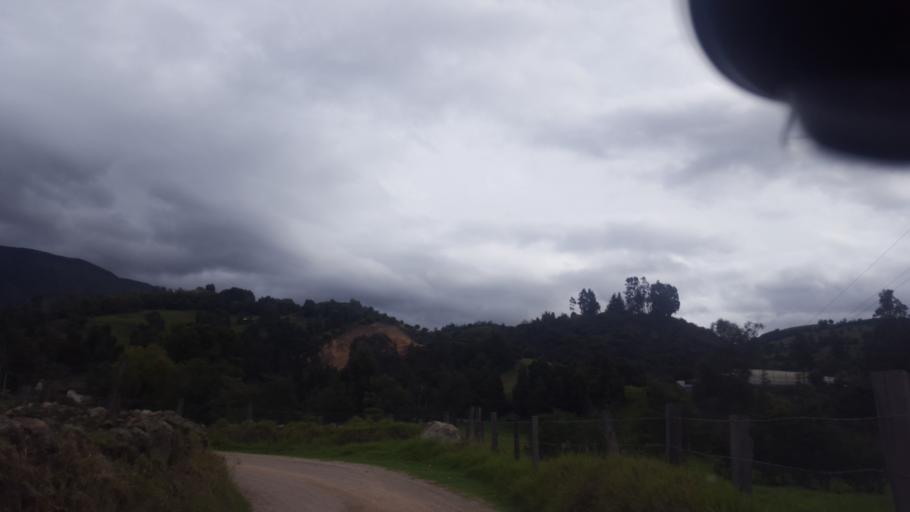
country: CO
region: Boyaca
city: Cerinza
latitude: 5.9800
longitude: -72.9446
